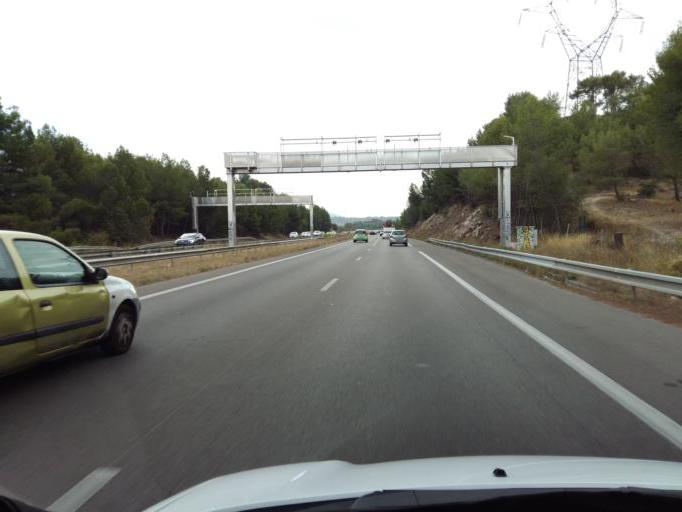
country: FR
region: Provence-Alpes-Cote d'Azur
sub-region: Departement des Bouches-du-Rhone
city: Cabries
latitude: 43.4471
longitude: 5.3957
